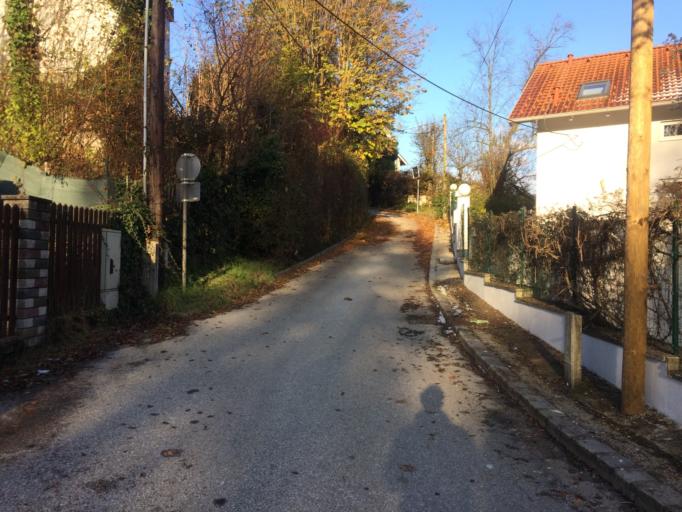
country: AT
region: Lower Austria
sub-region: Politischer Bezirk Wien-Umgebung
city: Gablitz
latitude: 48.2199
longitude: 16.1485
